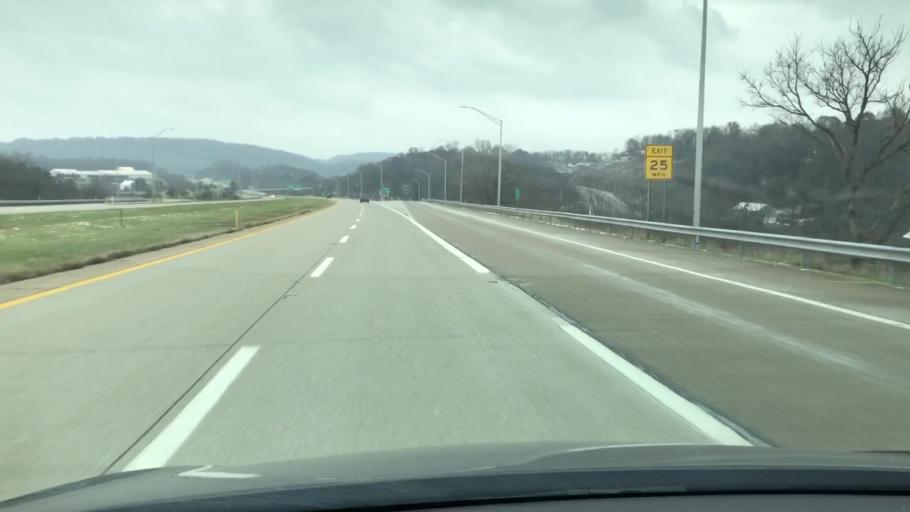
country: US
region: Pennsylvania
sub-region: Westmoreland County
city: New Stanton
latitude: 40.2391
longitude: -79.6057
